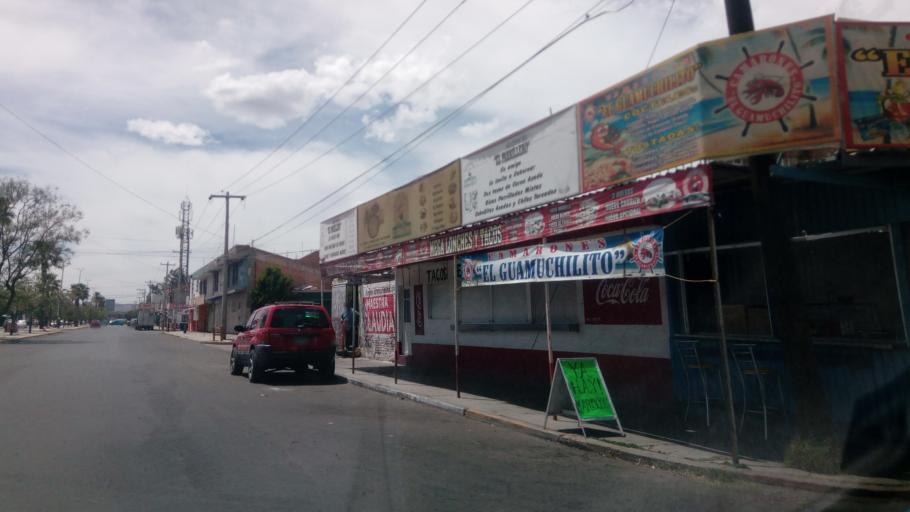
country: MX
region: Durango
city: Victoria de Durango
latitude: 23.9969
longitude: -104.6711
